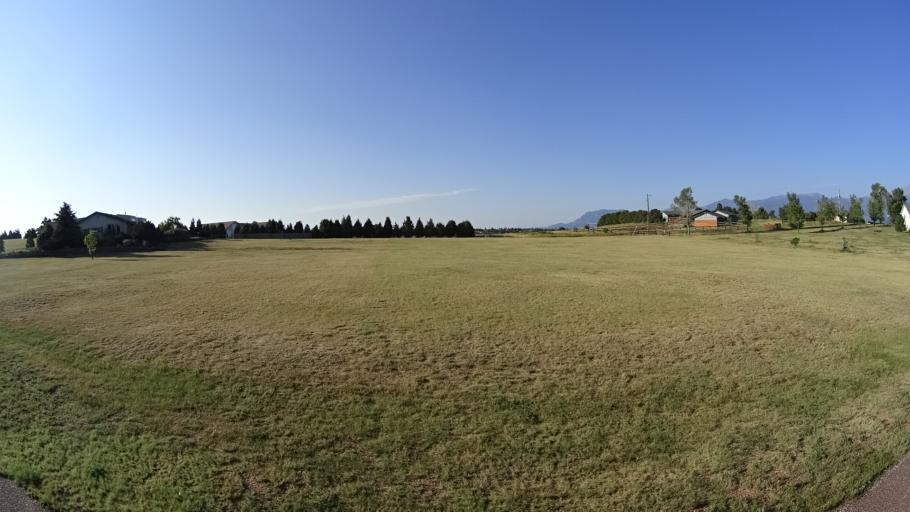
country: US
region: Colorado
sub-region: El Paso County
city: Black Forest
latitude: 38.9403
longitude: -104.7686
